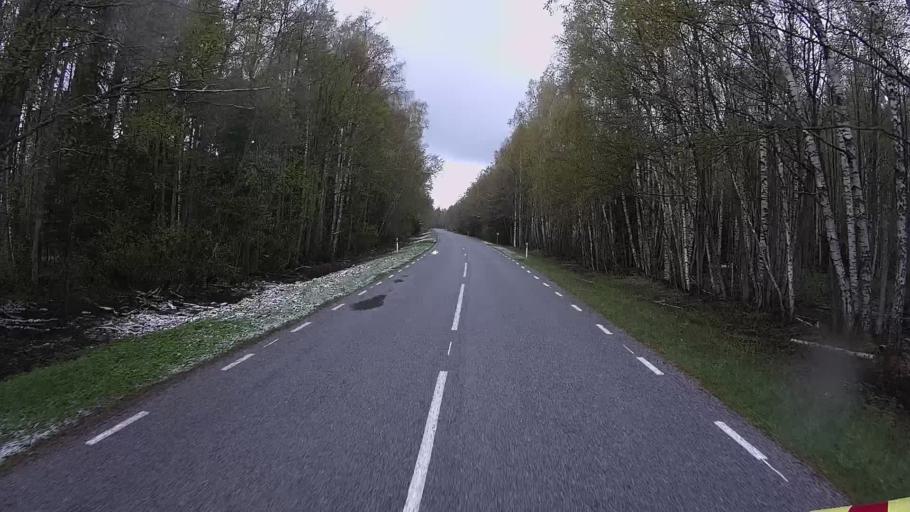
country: EE
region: Hiiumaa
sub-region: Kaerdla linn
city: Kardla
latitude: 58.7663
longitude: 22.5096
